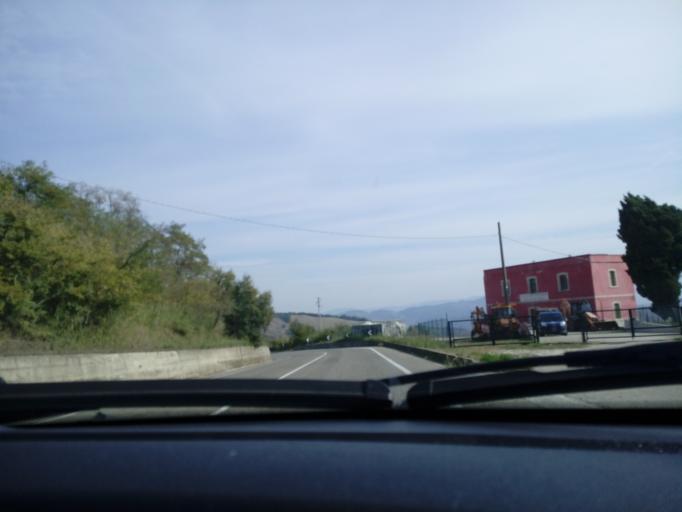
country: IT
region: Molise
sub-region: Provincia di Campobasso
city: Riccia
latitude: 41.5185
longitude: 14.8511
